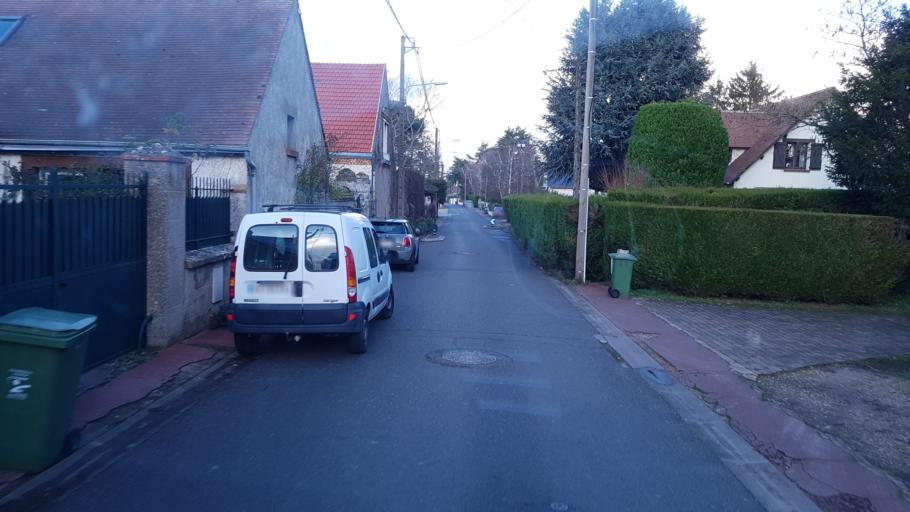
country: FR
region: Centre
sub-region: Departement du Loiret
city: Olivet
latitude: 47.8529
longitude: 1.9178
